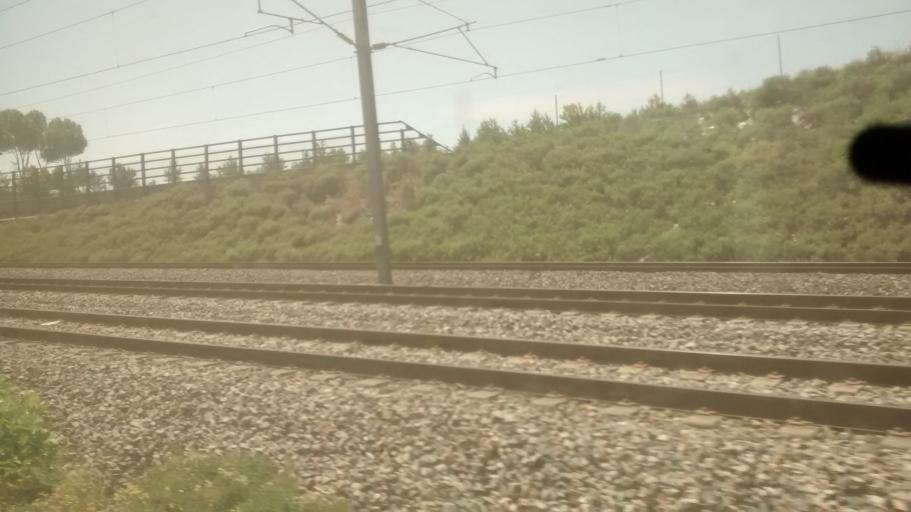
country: FR
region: Rhone-Alpes
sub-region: Departement de la Drome
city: Saint-Marcel-les-Valence
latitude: 44.9874
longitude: 4.9795
